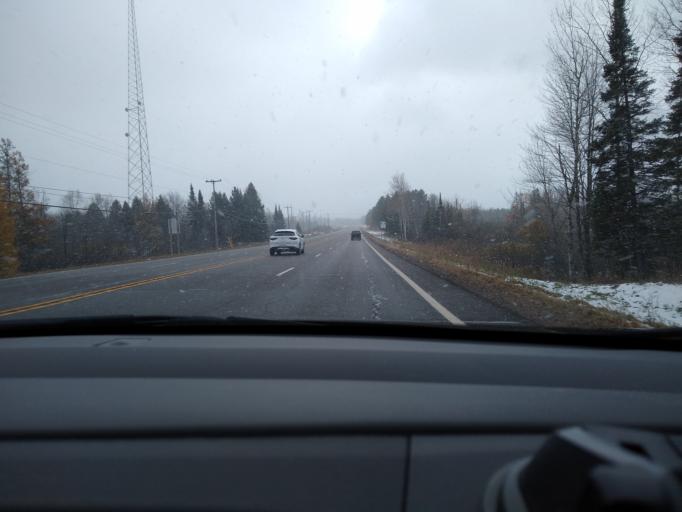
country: US
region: Michigan
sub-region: Dickinson County
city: Iron Mountain
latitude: 46.0448
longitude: -88.0618
